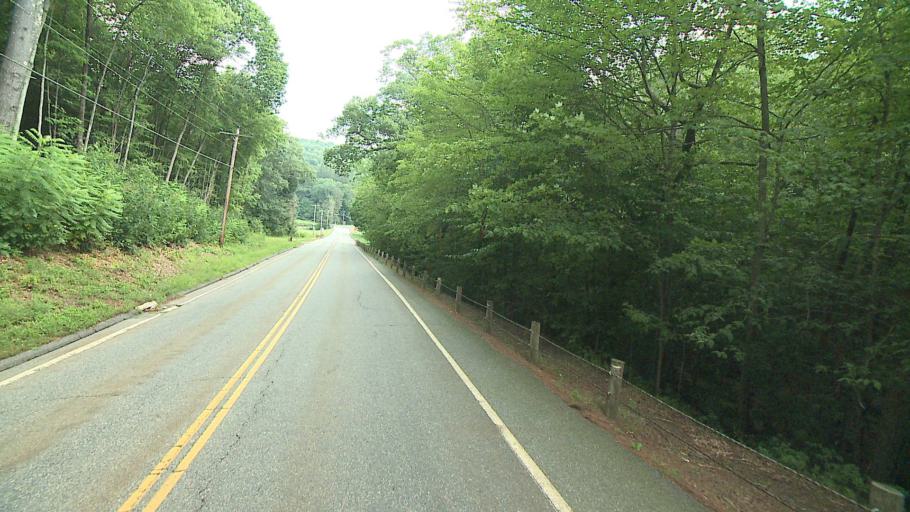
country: US
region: Connecticut
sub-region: Litchfield County
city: Bethlehem Village
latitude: 41.6729
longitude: -73.1460
